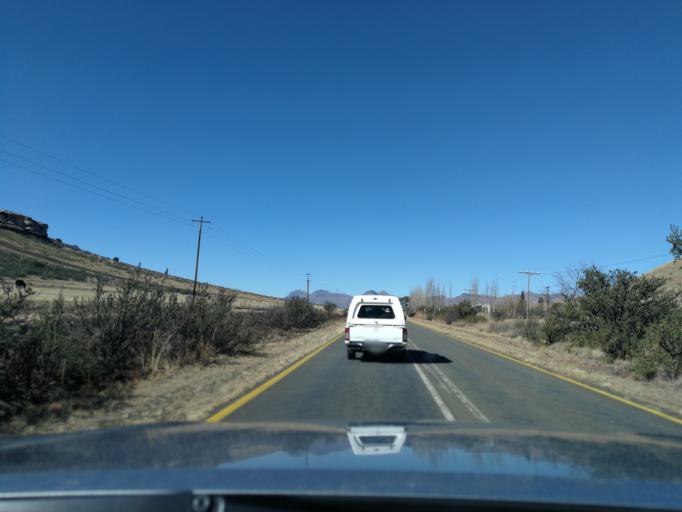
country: LS
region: Butha-Buthe
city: Butha-Buthe
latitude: -28.5192
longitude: 28.4435
